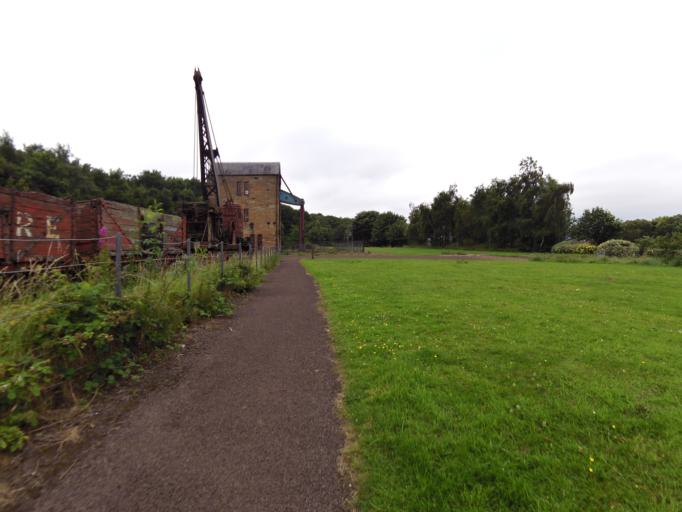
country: GB
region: Scotland
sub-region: East Lothian
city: Prestonpans
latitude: 55.9522
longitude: -3.0051
